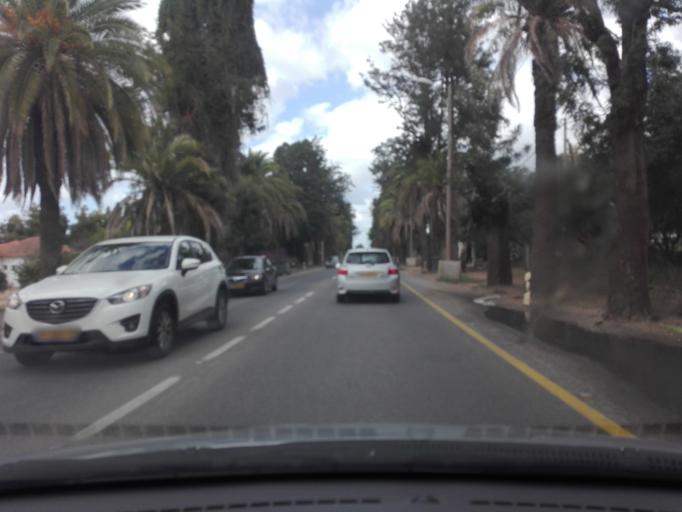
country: IL
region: Haifa
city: Hadera
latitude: 32.4783
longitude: 34.9750
